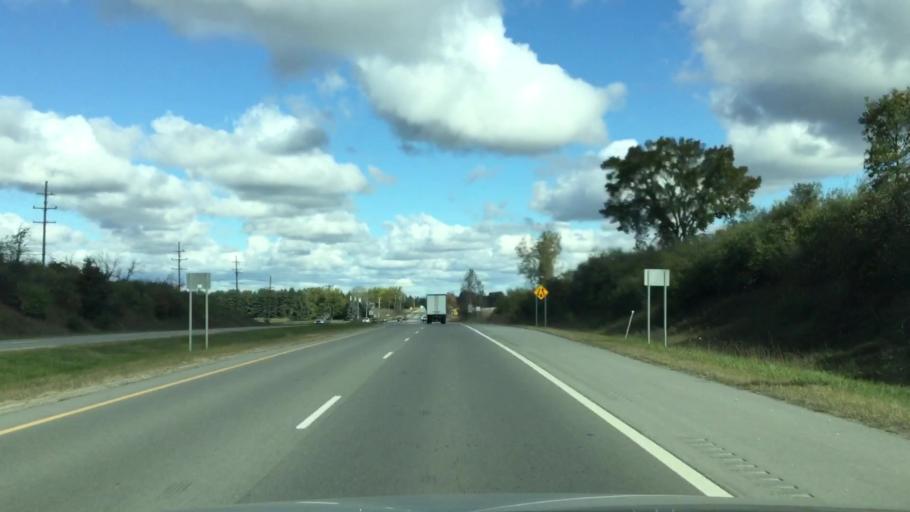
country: US
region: Michigan
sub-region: Oakland County
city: Oxford
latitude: 42.8958
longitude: -83.3114
